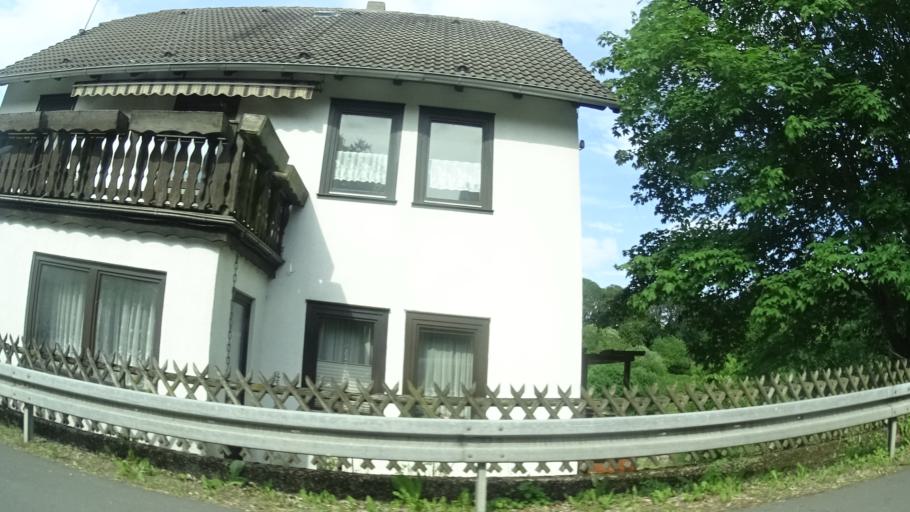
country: DE
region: Hesse
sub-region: Regierungsbezirk Kassel
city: Sachsenhausen
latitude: 51.2795
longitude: 9.0691
